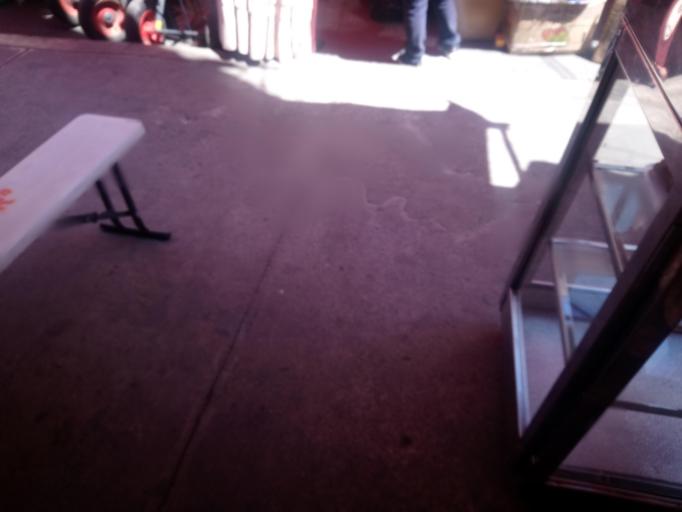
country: BO
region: La Paz
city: La Paz
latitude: -16.5014
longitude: -68.1393
